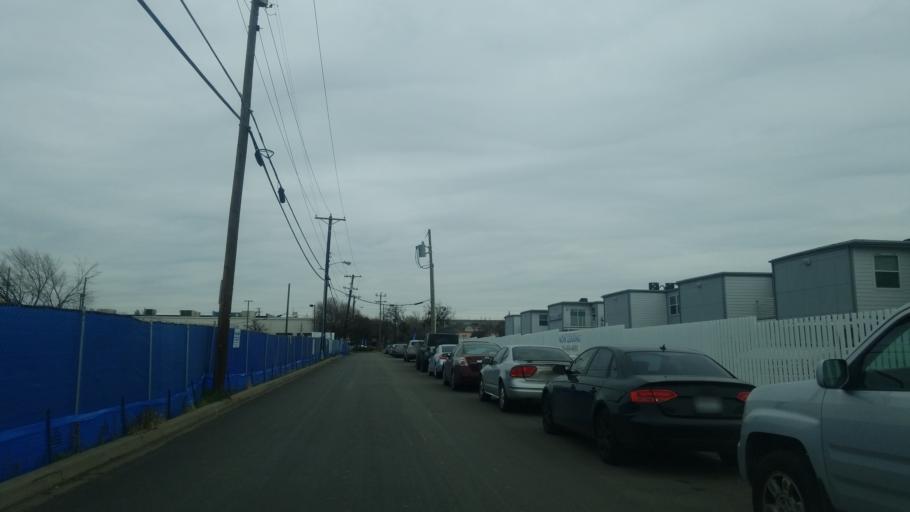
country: US
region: Texas
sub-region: Dallas County
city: Highland Park
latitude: 32.8244
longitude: -96.8235
